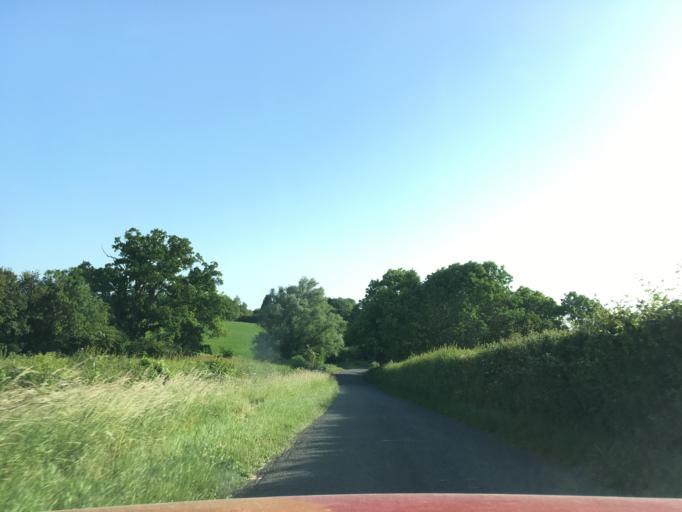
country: GB
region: England
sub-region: Gloucestershire
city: Fairford
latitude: 51.7377
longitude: -1.7366
